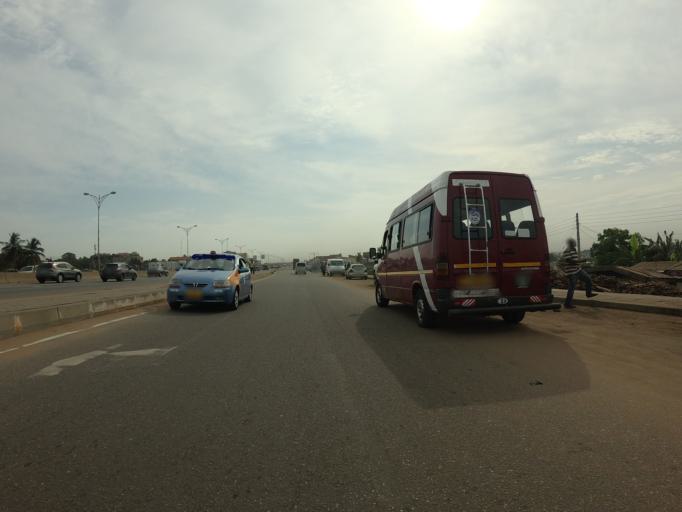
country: GH
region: Greater Accra
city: Dome
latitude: 5.6080
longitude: -0.2444
